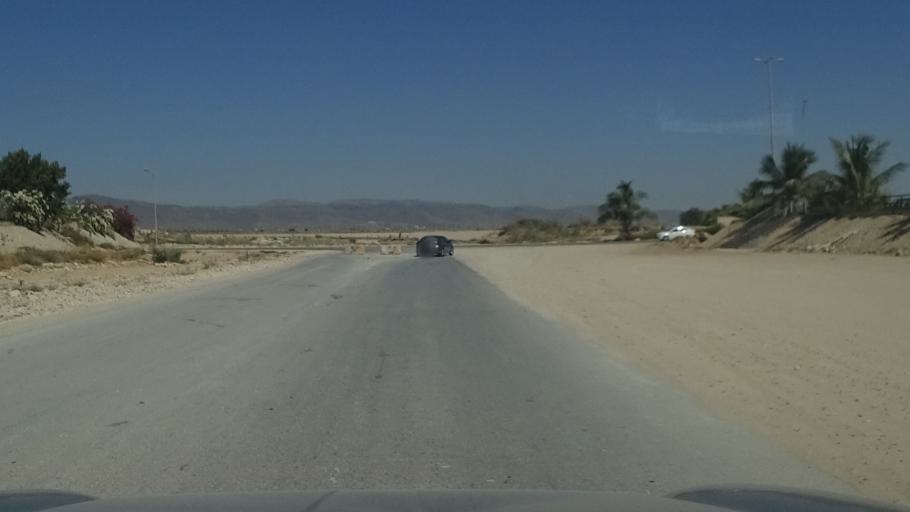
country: OM
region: Zufar
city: Salalah
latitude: 17.0226
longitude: 54.0633
